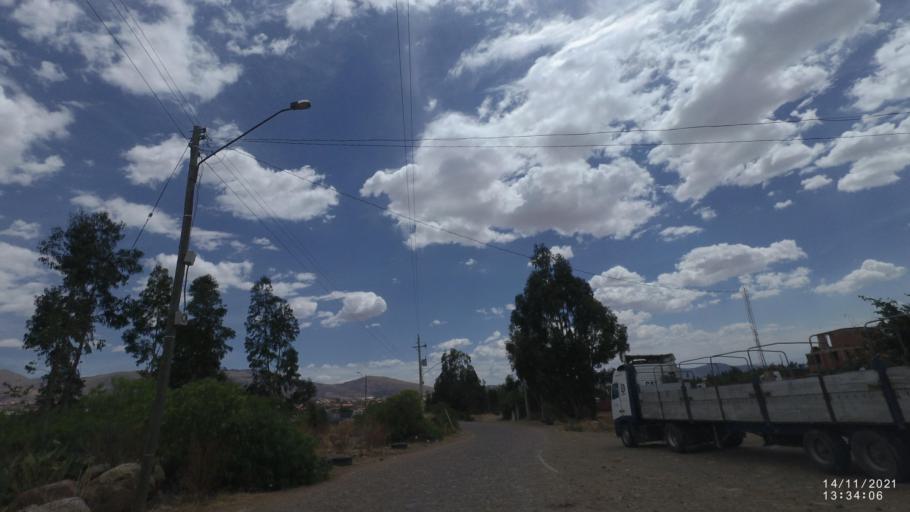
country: BO
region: Cochabamba
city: Colomi
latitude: -17.4009
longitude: -65.9837
